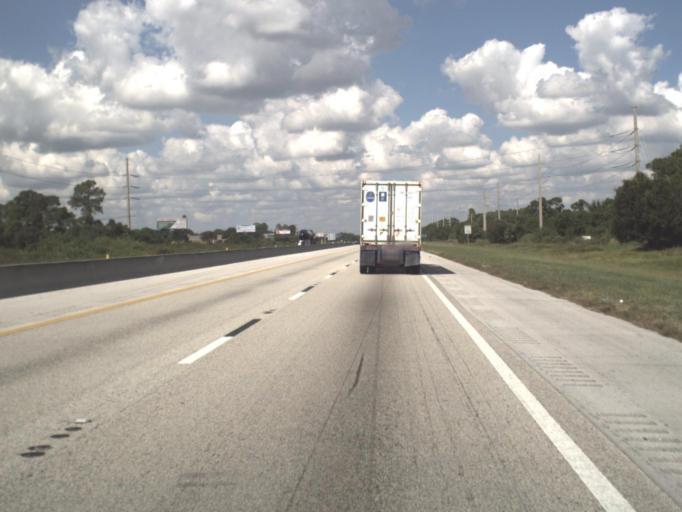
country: US
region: Florida
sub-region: Martin County
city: Palm City
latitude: 27.1638
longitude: -80.3062
